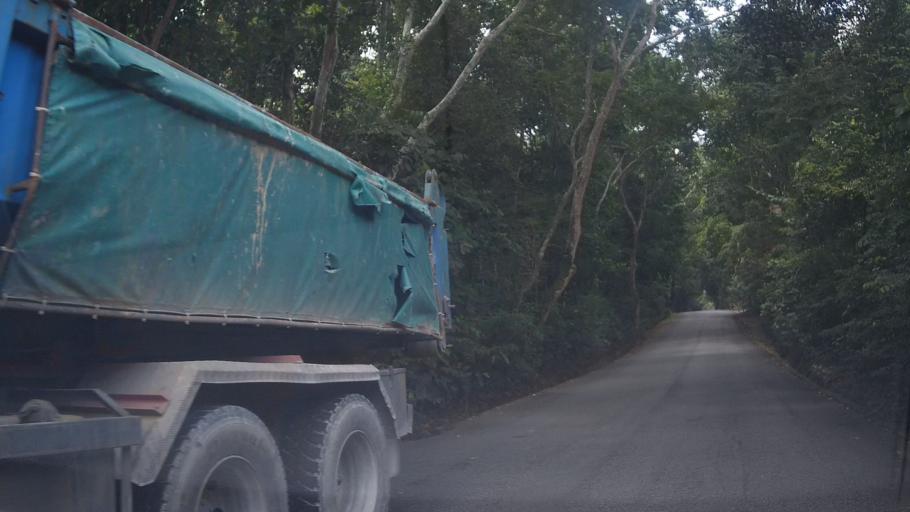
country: SG
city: Singapore
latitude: 1.3547
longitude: 103.7962
